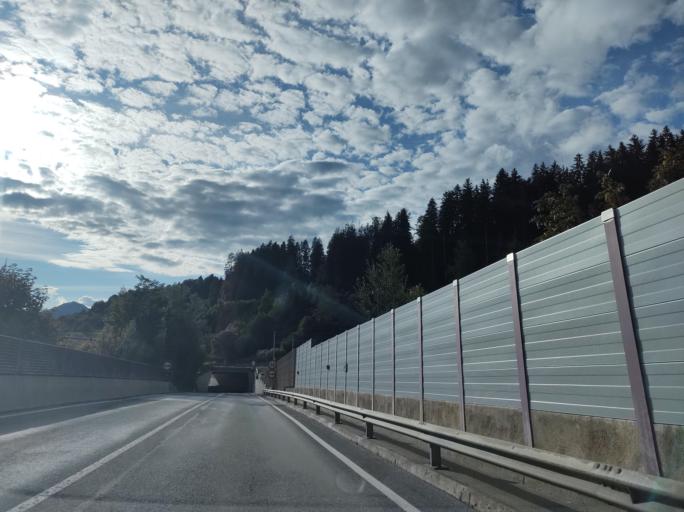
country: AT
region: Tyrol
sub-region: Politischer Bezirk Kitzbuhel
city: Kirchberg in Tirol
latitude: 47.4508
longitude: 12.3251
